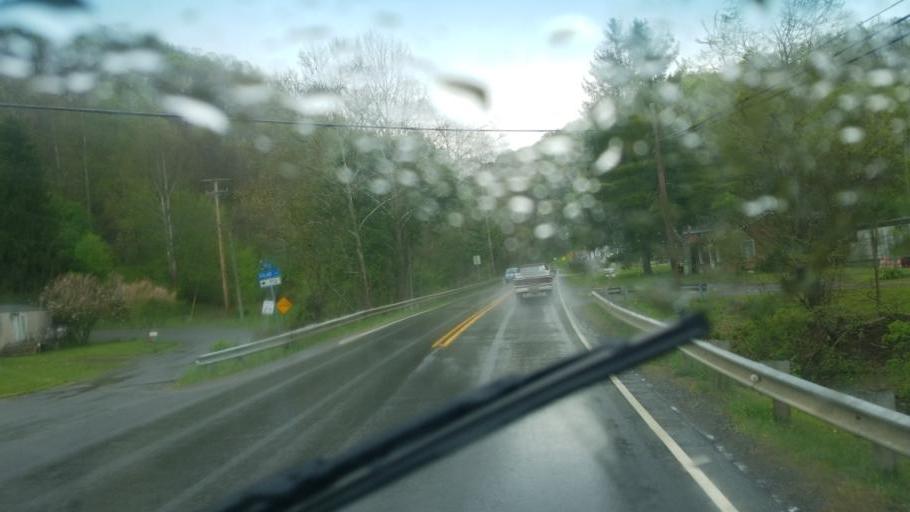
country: US
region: Virginia
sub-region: Smyth County
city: Marion
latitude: 36.8235
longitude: -81.4912
